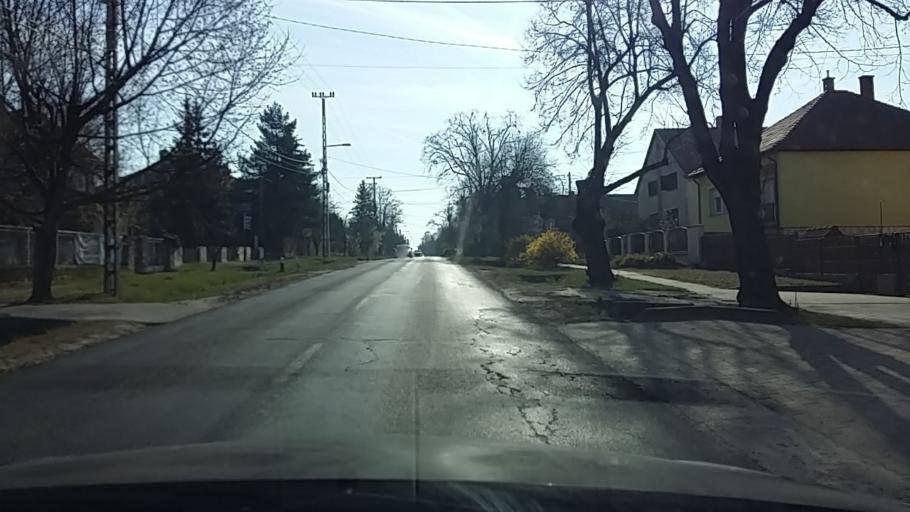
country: HU
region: Pest
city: Godollo
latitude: 47.5878
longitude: 19.3650
